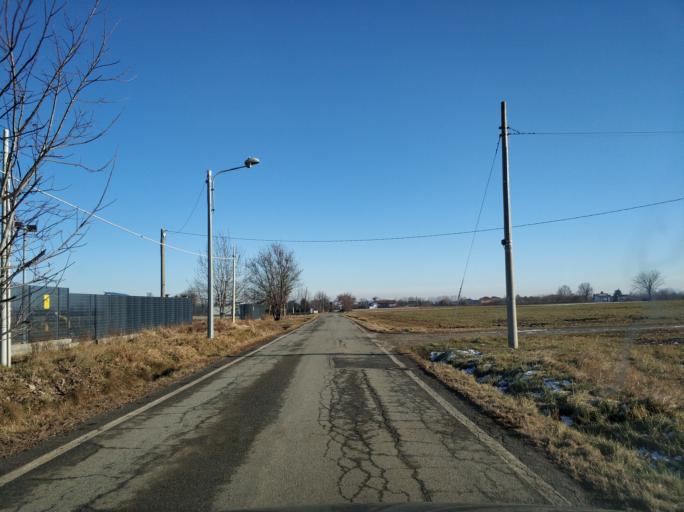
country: IT
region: Piedmont
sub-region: Provincia di Torino
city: San Carlo Canavese
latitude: 45.2423
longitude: 7.6278
